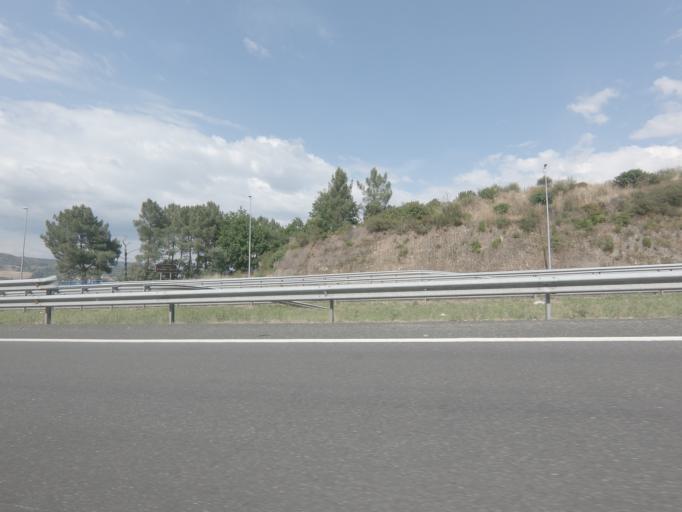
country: ES
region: Galicia
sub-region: Provincia de Ourense
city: Ourense
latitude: 42.3422
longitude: -7.8855
